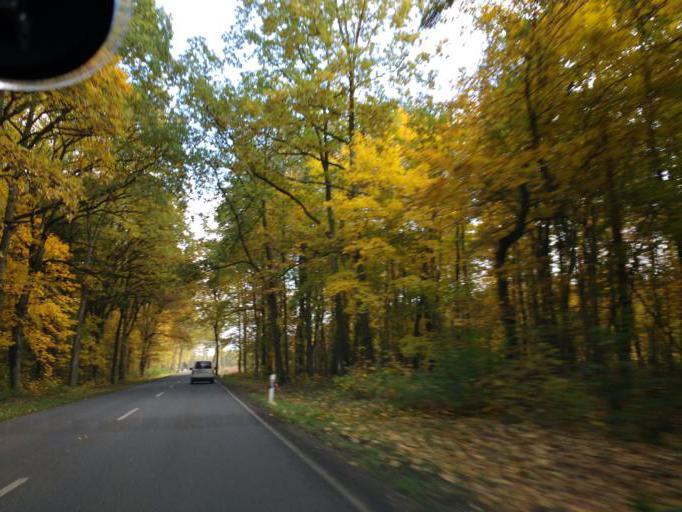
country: DE
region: Brandenburg
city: Petershagen
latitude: 52.5577
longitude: 13.7885
